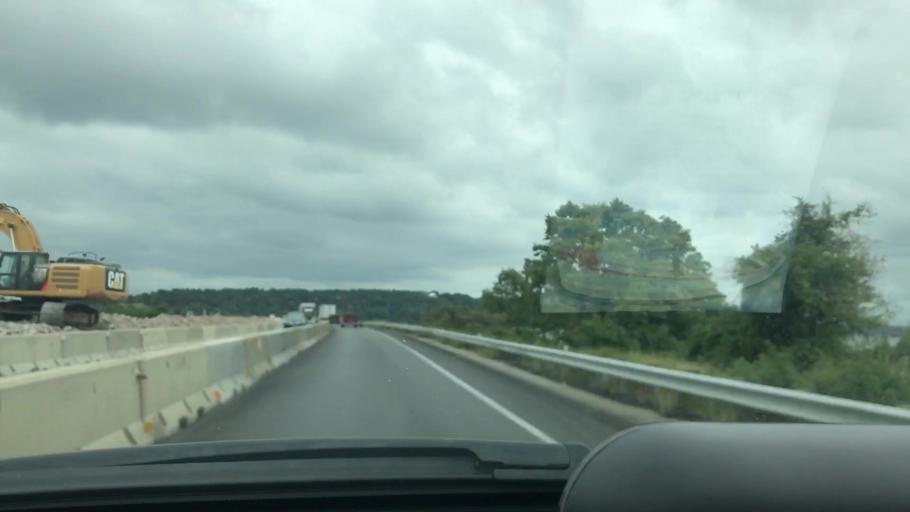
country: US
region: Oklahoma
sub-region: McIntosh County
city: Eufaula
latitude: 35.2382
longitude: -95.5898
